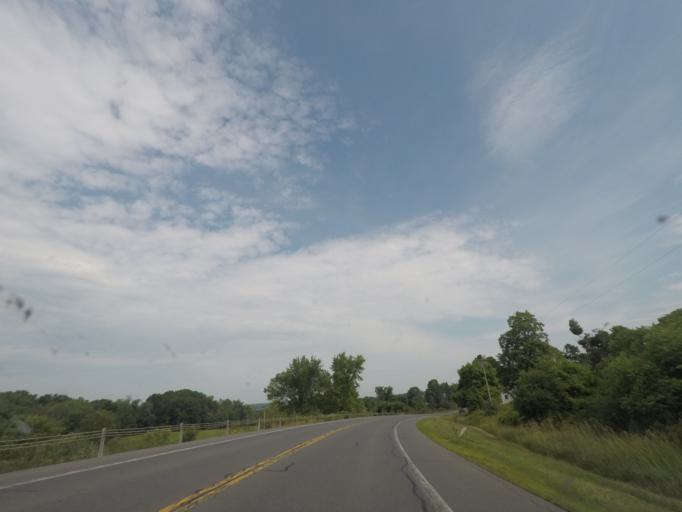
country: US
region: New York
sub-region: Rensselaer County
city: Poestenkill
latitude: 42.7011
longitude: -73.5616
